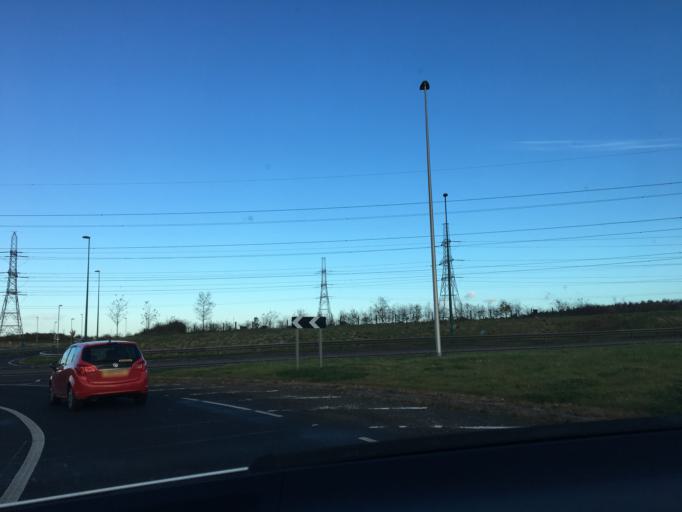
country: GB
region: Scotland
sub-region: Midlothian
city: Dalkeith
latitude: 55.9092
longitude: -3.0442
